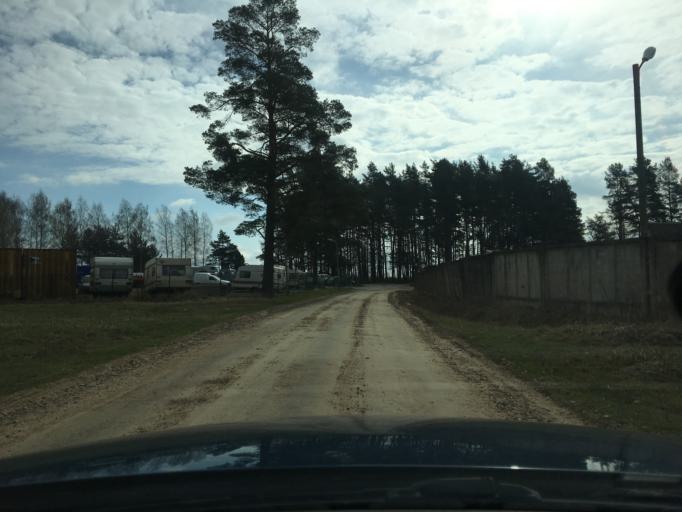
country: LV
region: Ikskile
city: Ikskile
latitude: 56.8229
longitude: 24.5300
